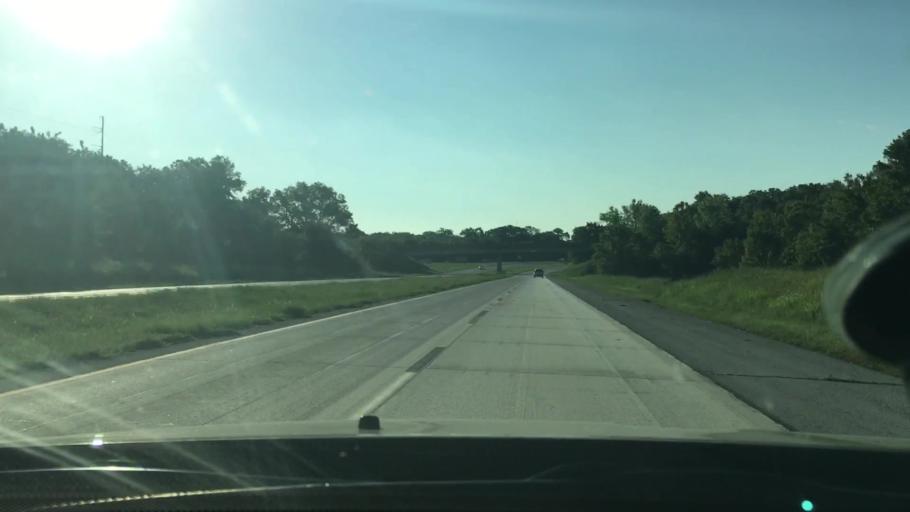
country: US
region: Oklahoma
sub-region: Pontotoc County
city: Ada
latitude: 34.7508
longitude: -96.6598
